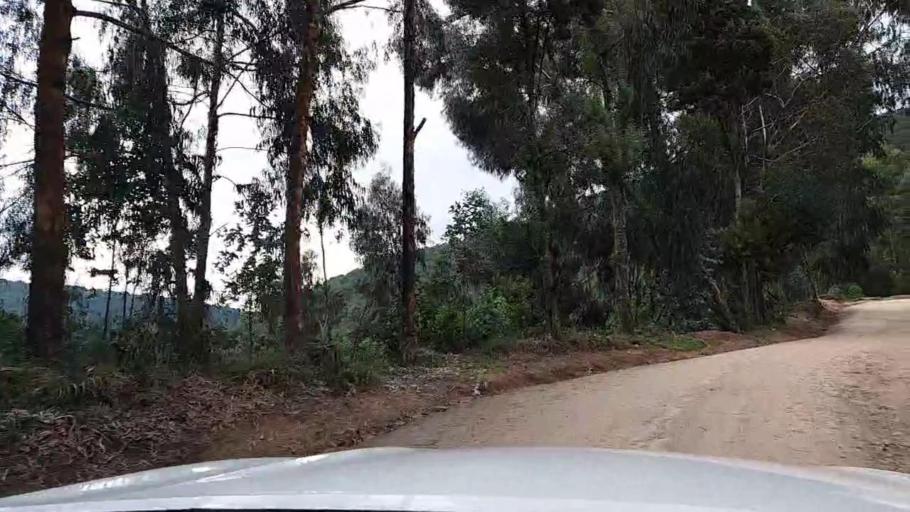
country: RW
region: Southern Province
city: Nzega
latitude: -2.3841
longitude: 29.3845
